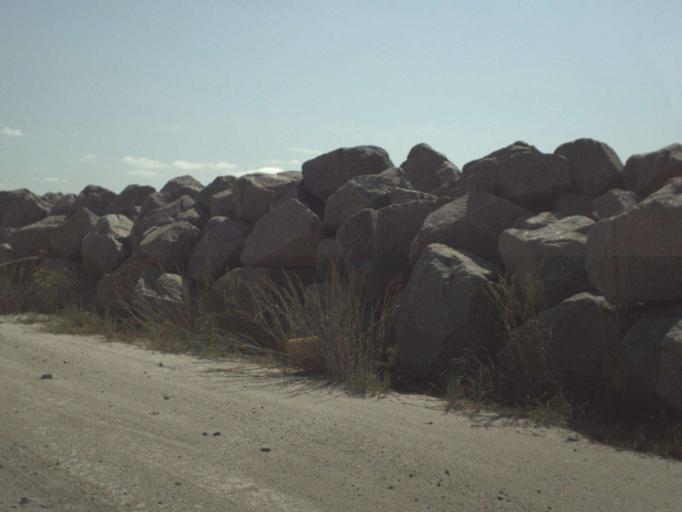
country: US
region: Florida
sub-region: Gulf County
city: Port Saint Joe
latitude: 29.6784
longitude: -85.3653
